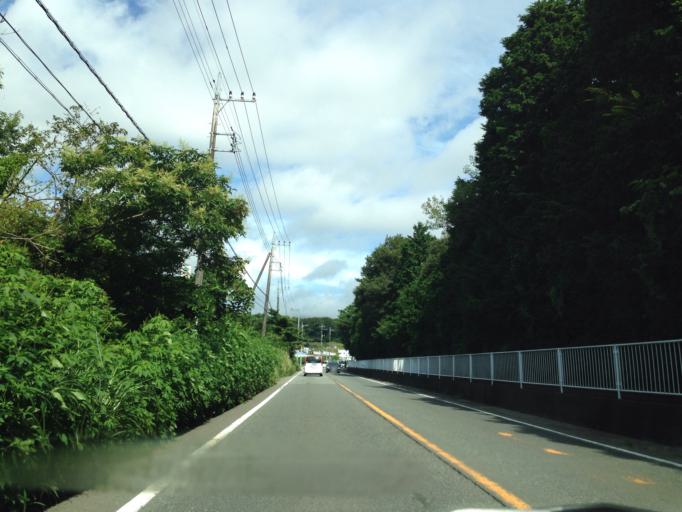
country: JP
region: Shizuoka
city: Gotemba
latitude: 35.3454
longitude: 138.8816
